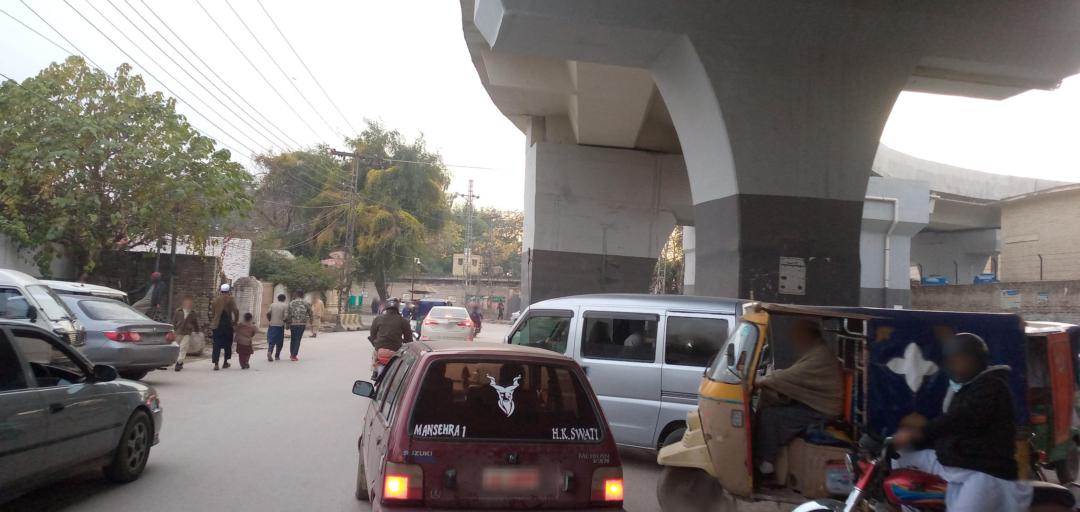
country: PK
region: Khyber Pakhtunkhwa
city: Peshawar
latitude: 33.9945
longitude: 71.5377
